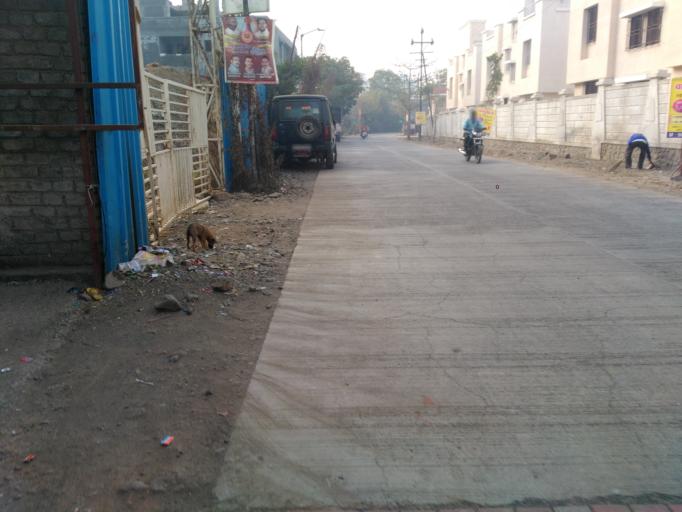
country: IN
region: Maharashtra
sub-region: Pune Division
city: Pune
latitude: 18.4552
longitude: 73.9125
